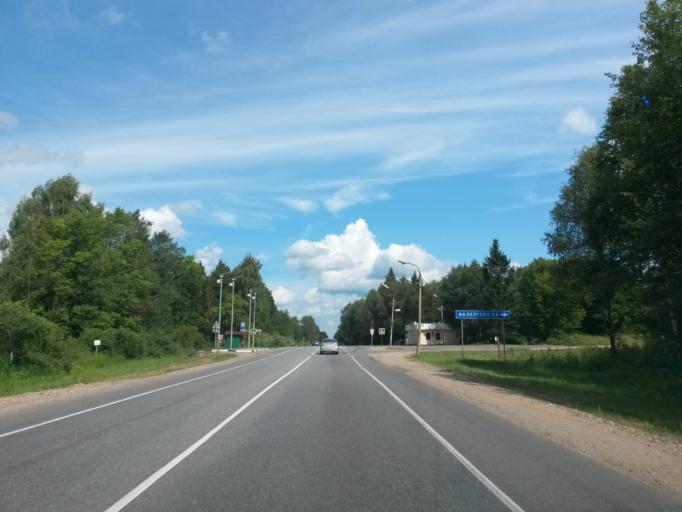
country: RU
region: Jaroslavl
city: Pereslavl'-Zalesskiy
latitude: 56.7918
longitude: 38.8882
